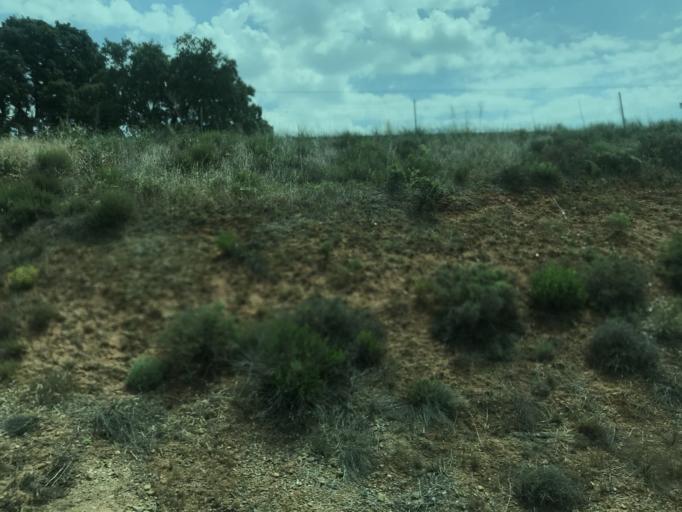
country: ES
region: Castille and Leon
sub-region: Provincia de Burgos
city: Madrigalejo del Monte
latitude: 42.1113
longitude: -3.7178
